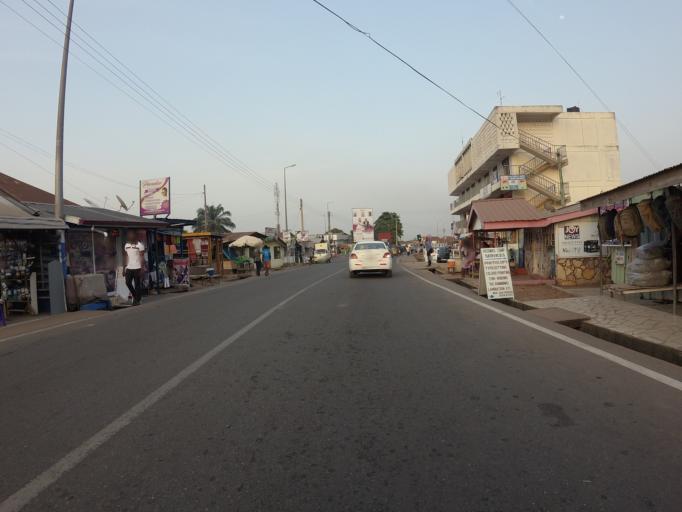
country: GH
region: Volta
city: Ho
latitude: 6.6066
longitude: 0.4721
